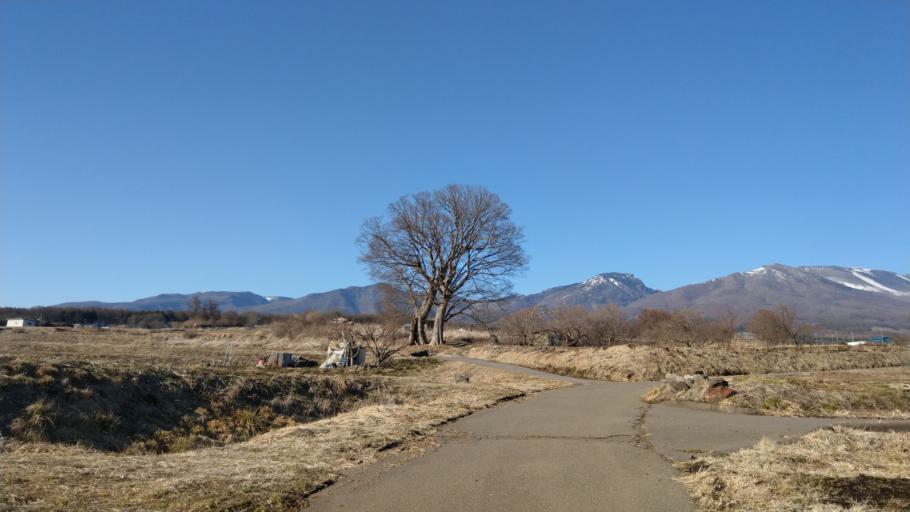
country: JP
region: Nagano
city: Komoro
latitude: 36.3275
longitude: 138.4678
